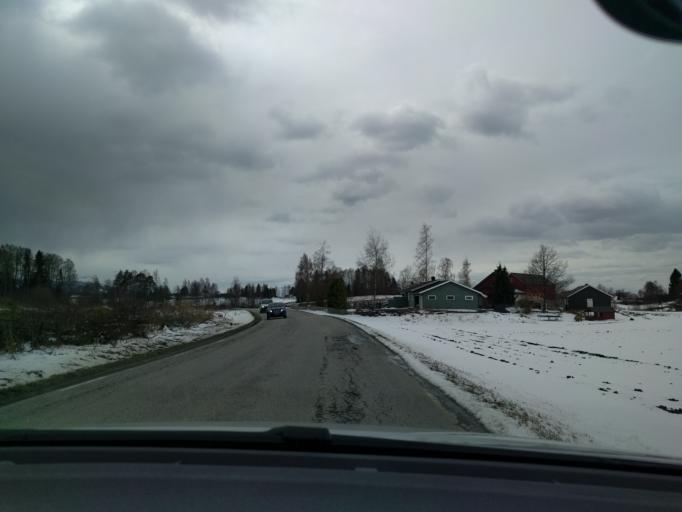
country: NO
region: Hedmark
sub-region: Stange
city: Stange
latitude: 60.7133
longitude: 11.1578
